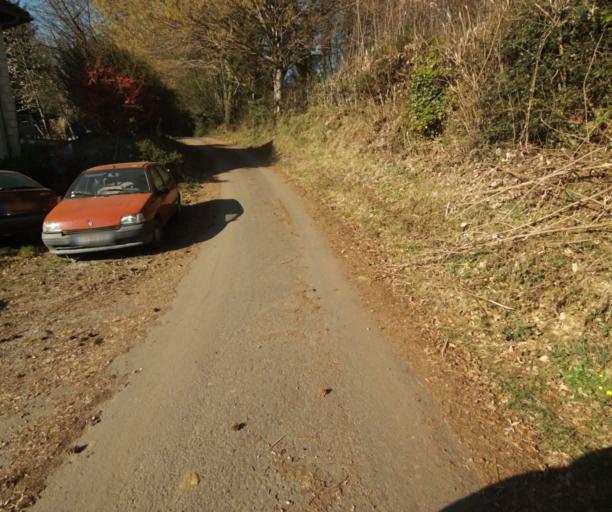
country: FR
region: Limousin
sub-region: Departement de la Correze
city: Saint-Clement
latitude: 45.3403
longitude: 1.6810
